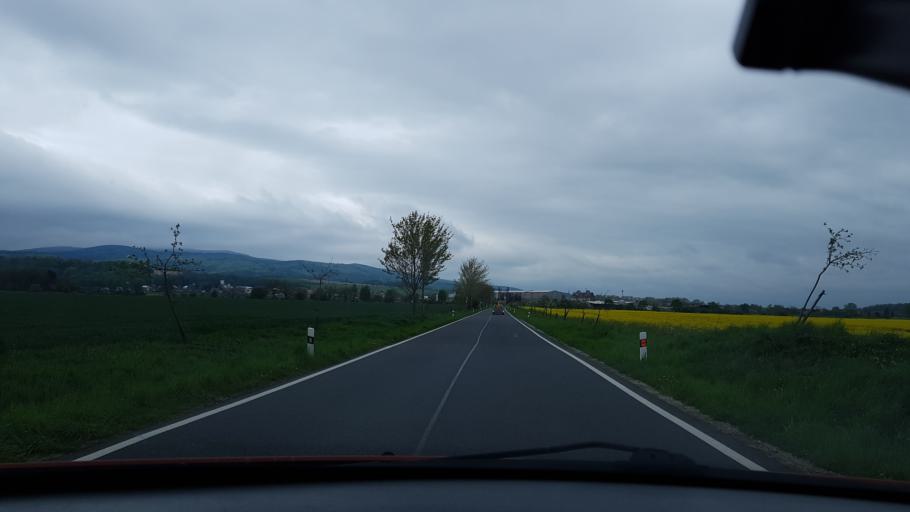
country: CZ
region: Olomoucky
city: Javornik
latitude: 50.3894
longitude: 17.0308
